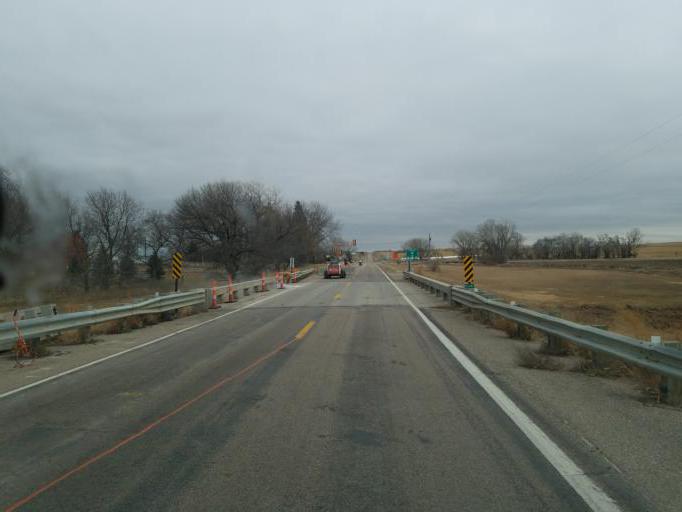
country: US
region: Nebraska
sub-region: Cedar County
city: Hartington
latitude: 42.6128
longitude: -97.4309
